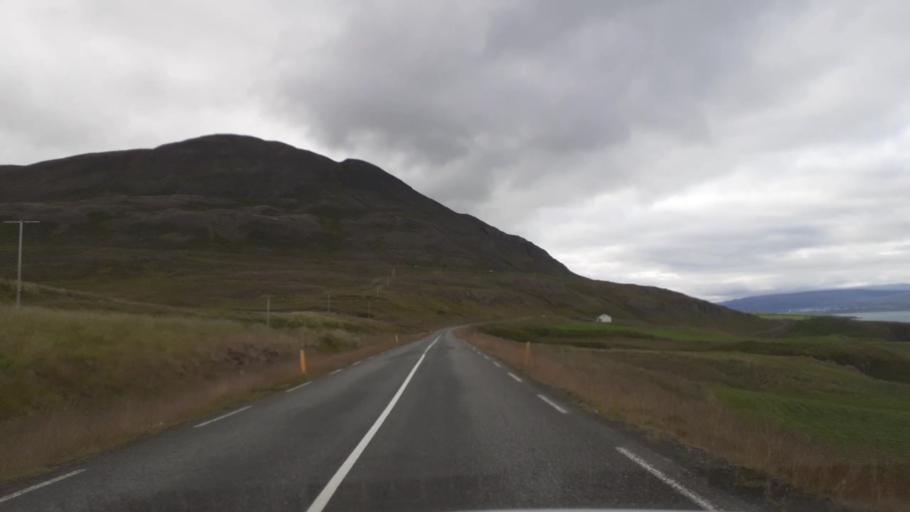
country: IS
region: Northeast
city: Akureyri
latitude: 65.8194
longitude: -18.0498
